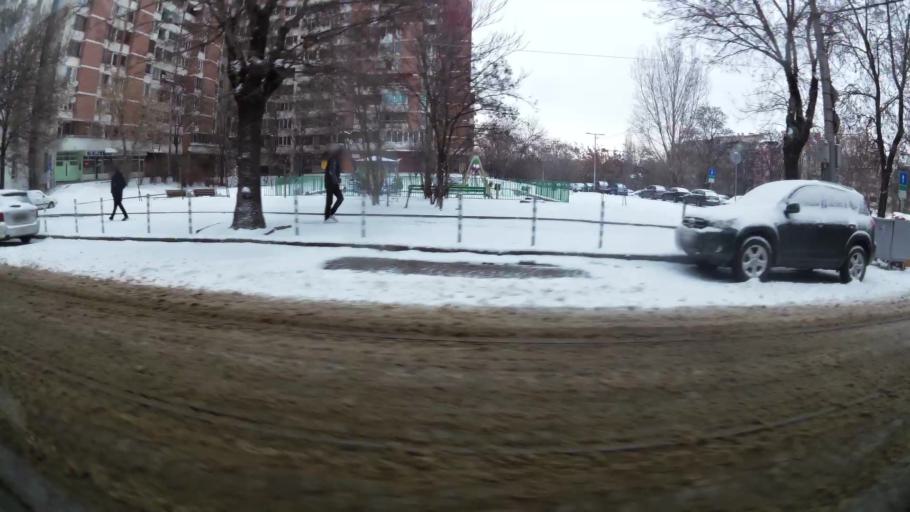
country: BG
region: Sofia-Capital
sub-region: Stolichna Obshtina
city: Sofia
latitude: 42.7025
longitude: 23.3031
